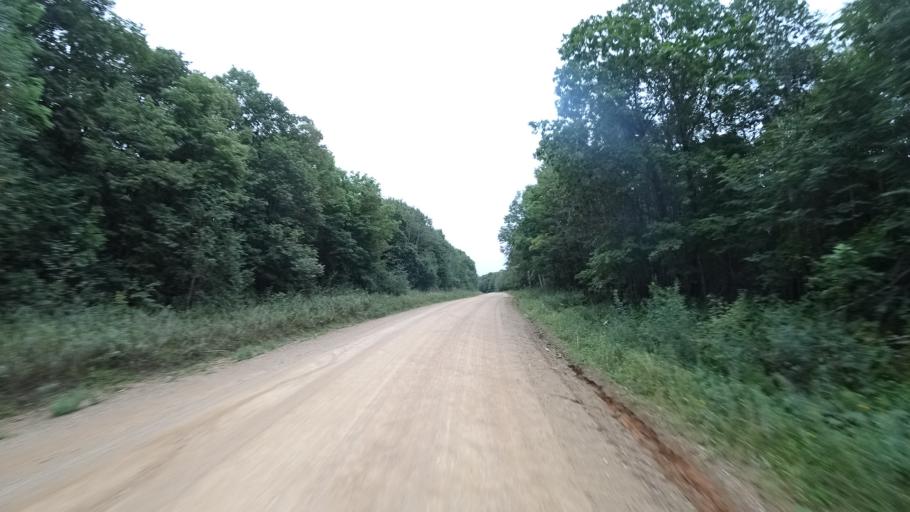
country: RU
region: Primorskiy
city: Rettikhovka
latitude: 44.1844
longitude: 132.8192
